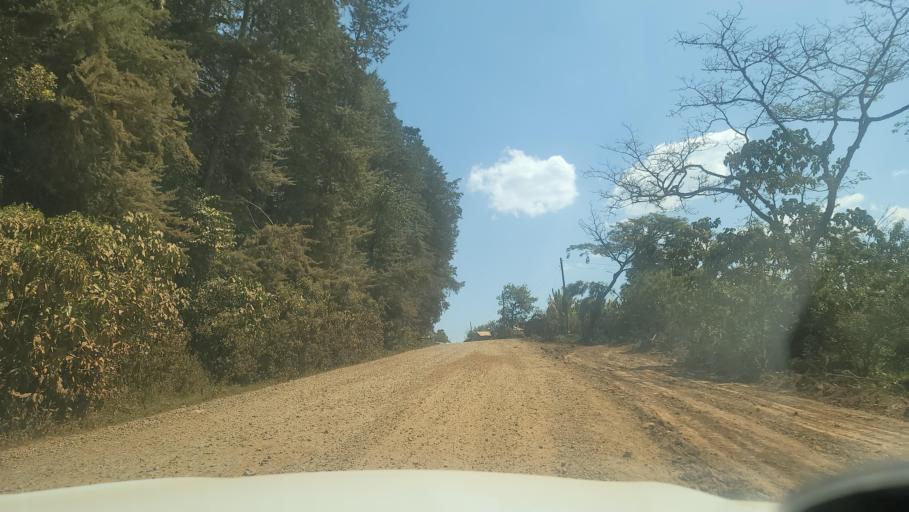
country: ET
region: Oromiya
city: Agaro
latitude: 7.7851
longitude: 36.4098
